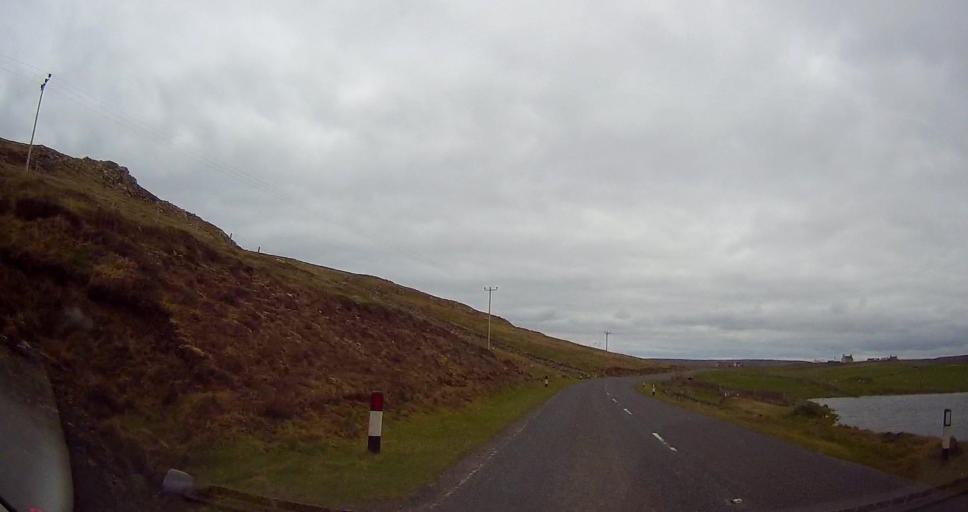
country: GB
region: Scotland
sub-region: Shetland Islands
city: Shetland
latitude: 60.6921
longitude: -0.9568
